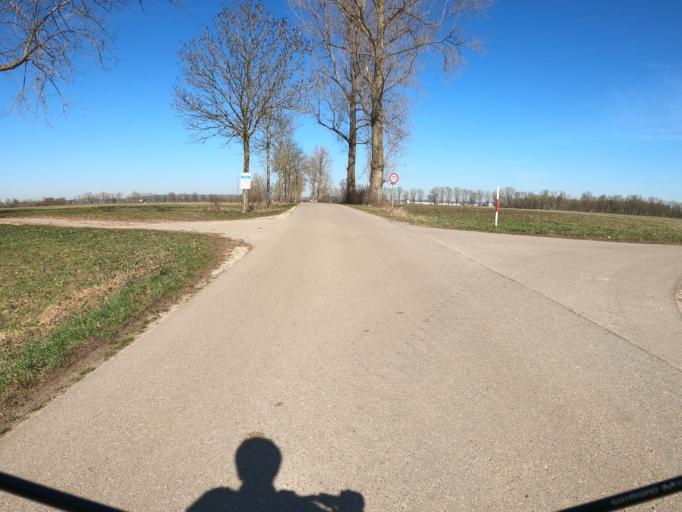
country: DE
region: Baden-Wuerttemberg
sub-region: Tuebingen Region
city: Langenau
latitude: 48.4741
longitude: 10.1359
